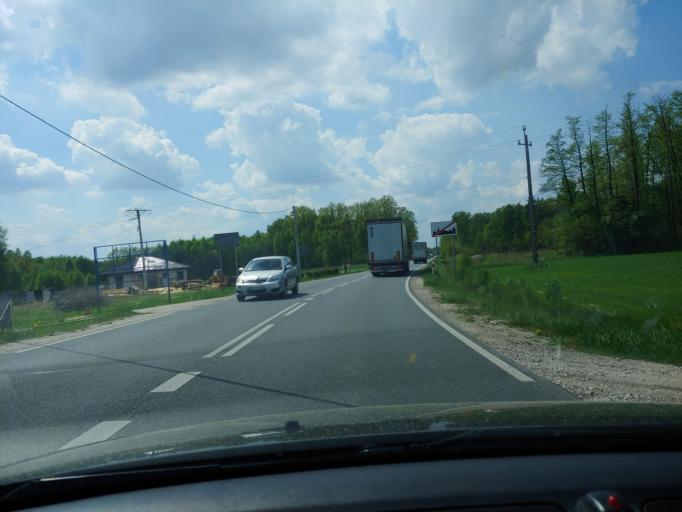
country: PL
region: Lesser Poland Voivodeship
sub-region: Powiat tarnowski
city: Lisia Gora
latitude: 50.0882
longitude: 21.0796
